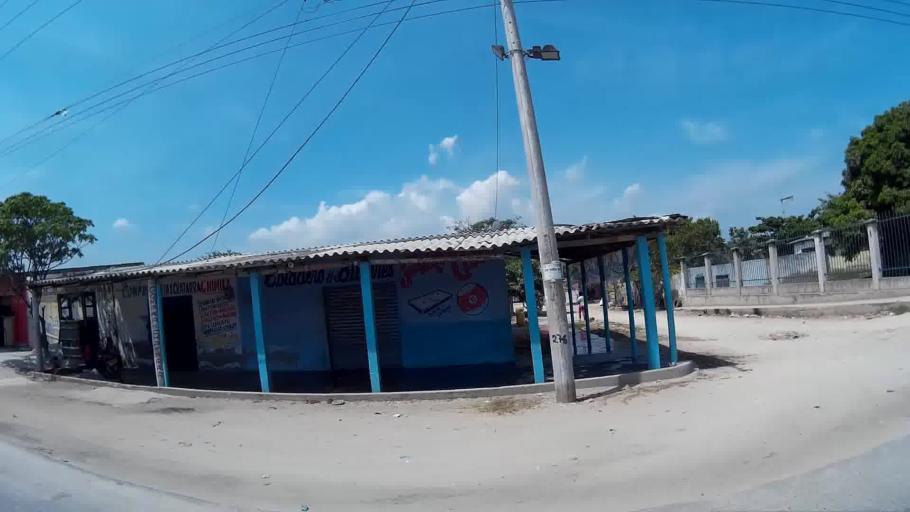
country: CO
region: Magdalena
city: Cienaga
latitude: 11.0052
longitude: -74.2375
